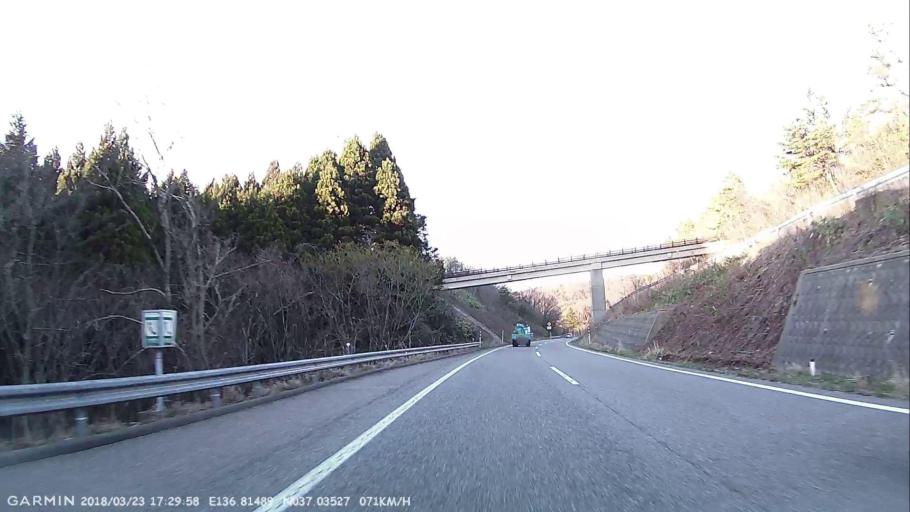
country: JP
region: Ishikawa
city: Nanao
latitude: 37.0354
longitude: 136.8150
